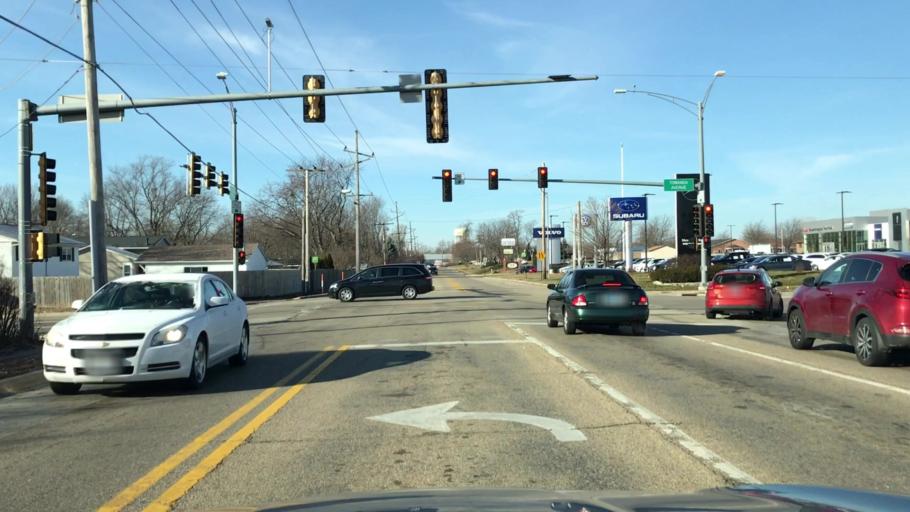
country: US
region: Illinois
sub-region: McLean County
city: Normal
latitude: 40.5177
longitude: -88.9604
